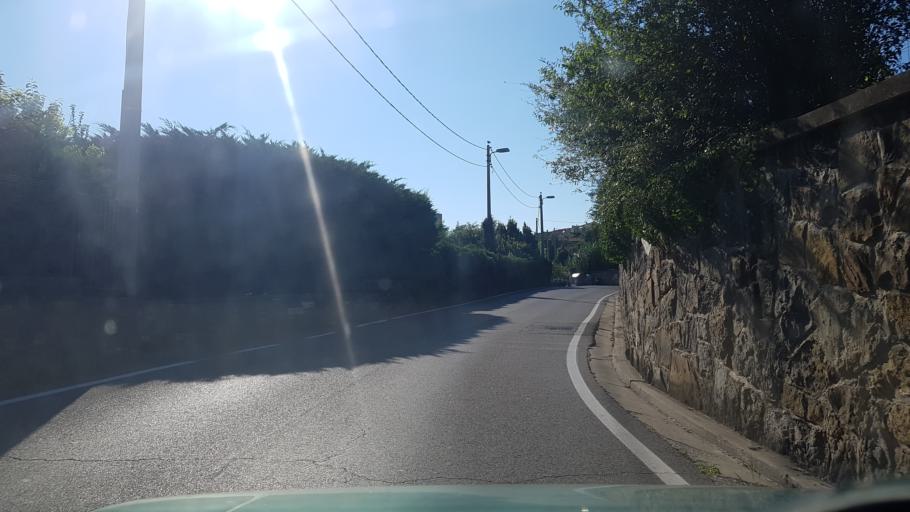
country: IT
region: Friuli Venezia Giulia
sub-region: Provincia di Trieste
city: Domio
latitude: 45.6241
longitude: 13.8139
